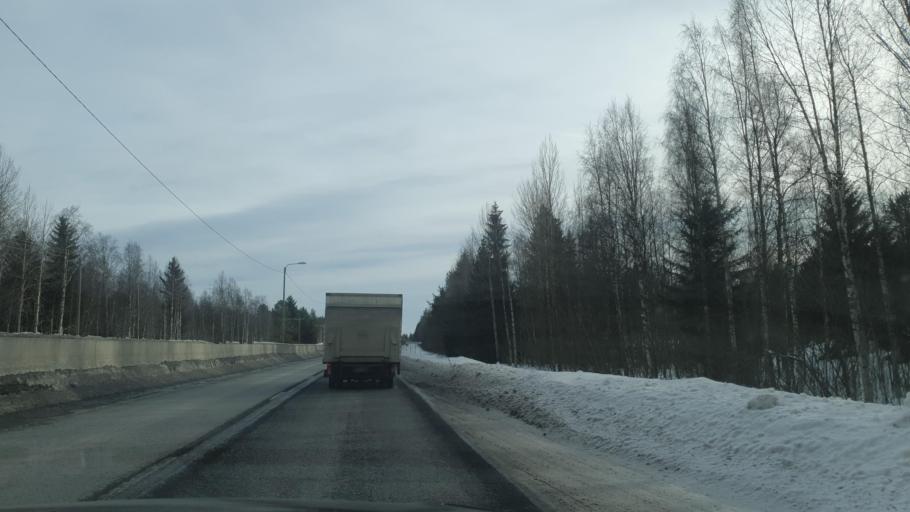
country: FI
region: Northern Ostrobothnia
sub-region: Oulu
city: Kempele
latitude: 64.9667
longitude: 25.6292
